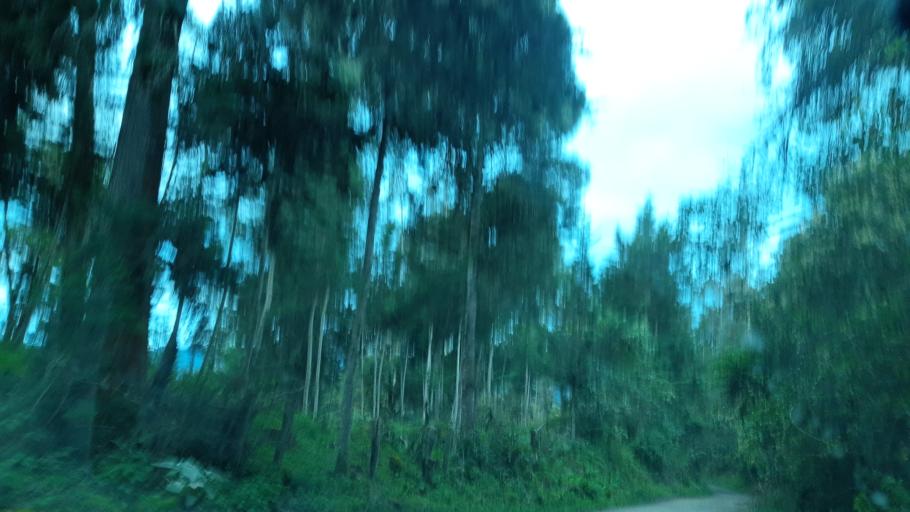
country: CO
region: Boyaca
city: Garagoa
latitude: 5.0930
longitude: -73.3341
